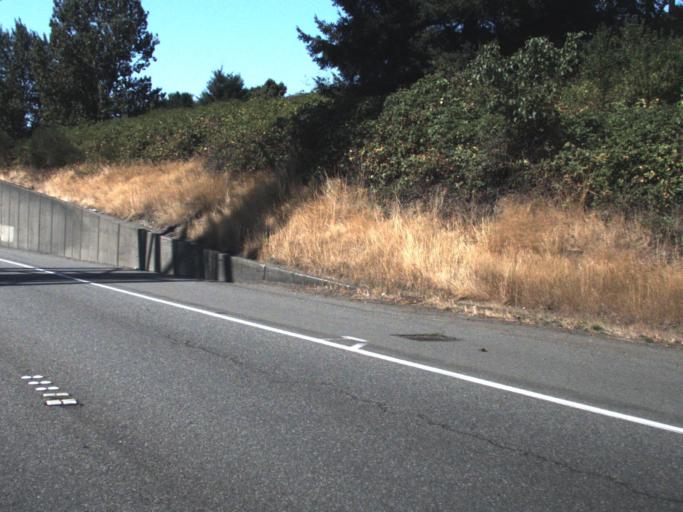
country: US
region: Washington
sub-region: King County
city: Riverton
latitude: 47.4688
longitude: -122.3073
